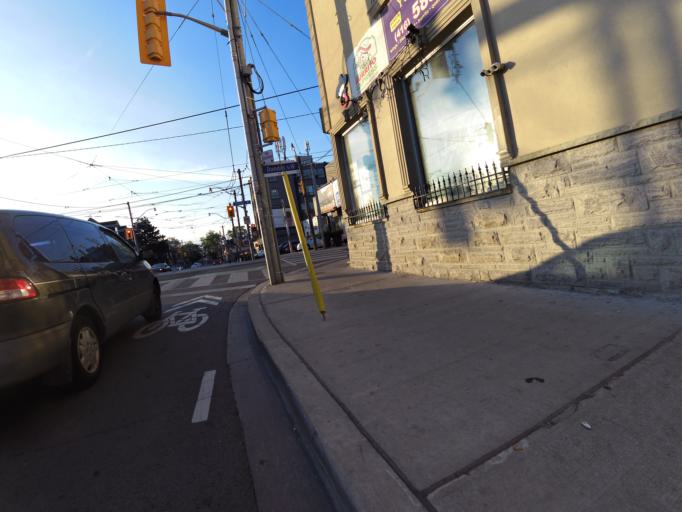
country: CA
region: Ontario
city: Toronto
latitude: 43.6500
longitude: -79.4396
